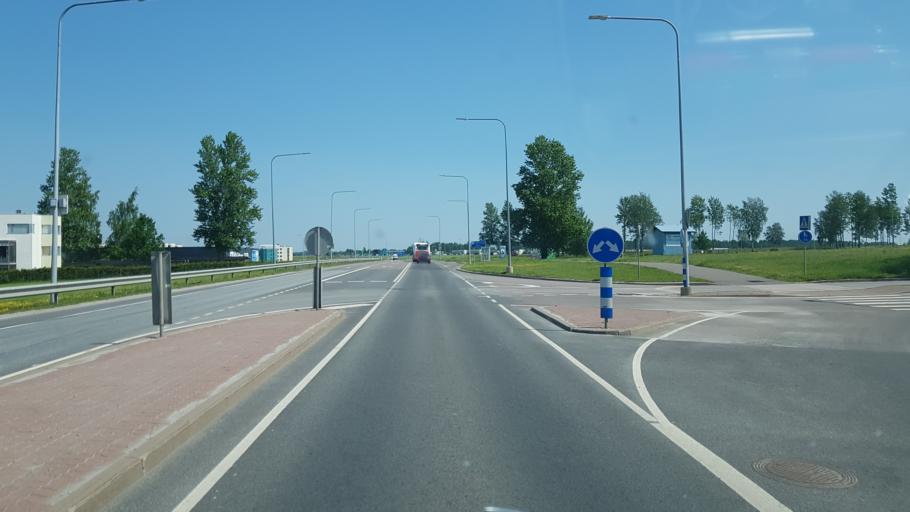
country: EE
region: Tartu
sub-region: Tartu linn
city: Tartu
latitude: 58.4010
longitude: 26.7403
